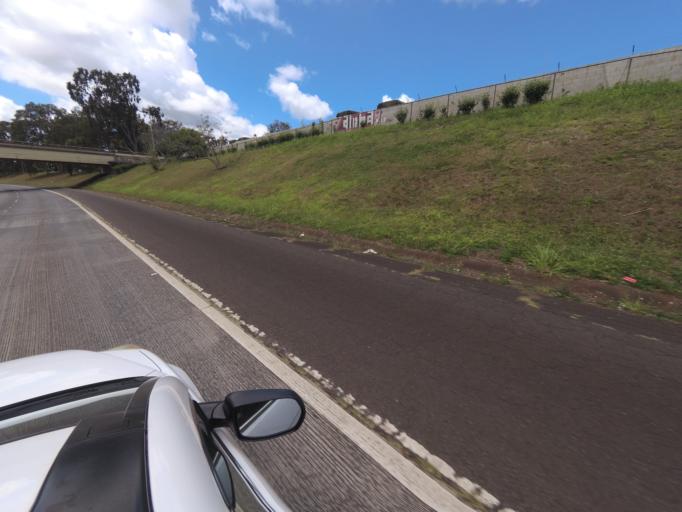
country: US
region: Hawaii
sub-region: Honolulu County
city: Waipi'o Acres
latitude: 21.4809
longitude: -158.0247
